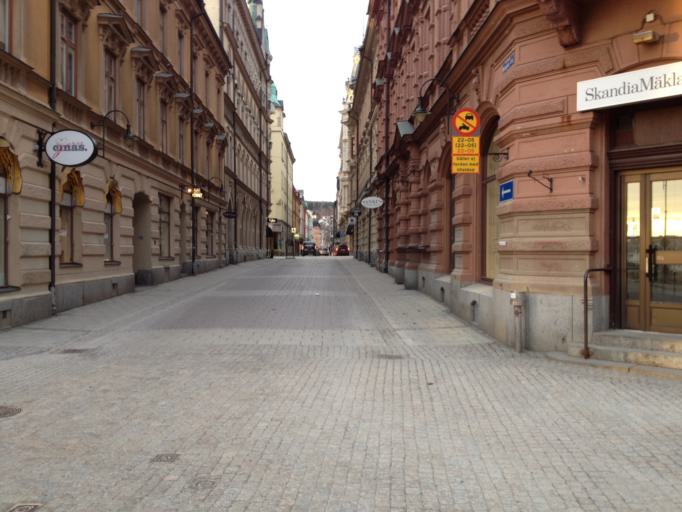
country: SE
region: Vaesternorrland
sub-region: Sundsvalls Kommun
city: Sundsvall
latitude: 62.3913
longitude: 17.3117
